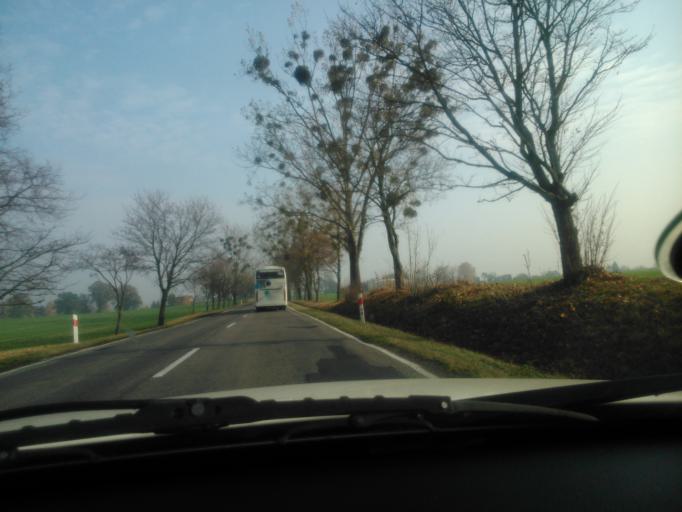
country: PL
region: Kujawsko-Pomorskie
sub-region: Powiat brodnicki
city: Bobrowo
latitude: 53.2328
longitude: 19.2479
